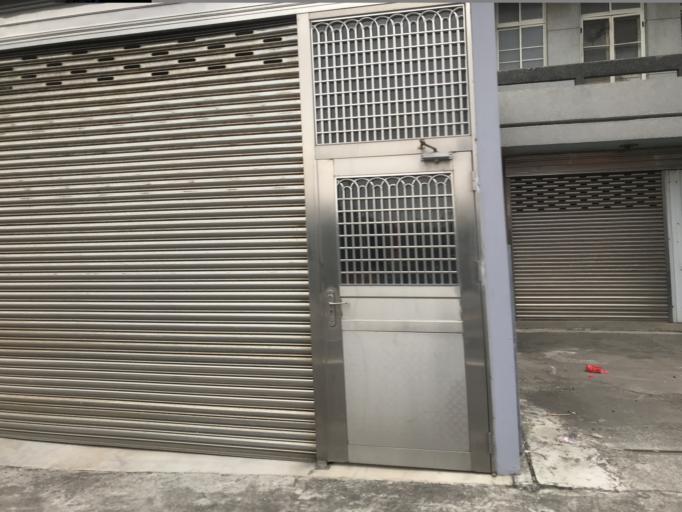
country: TW
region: Taiwan
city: Fengyuan
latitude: 24.3568
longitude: 120.6079
